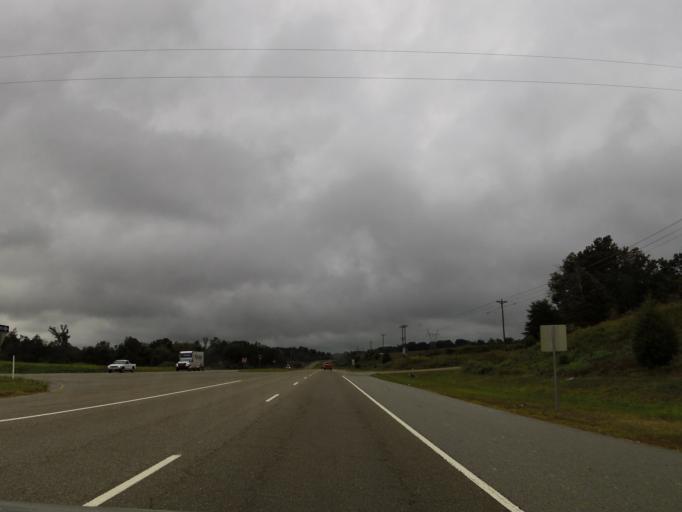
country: US
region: Tennessee
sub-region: Loudon County
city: Greenback
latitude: 35.7374
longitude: -84.1854
